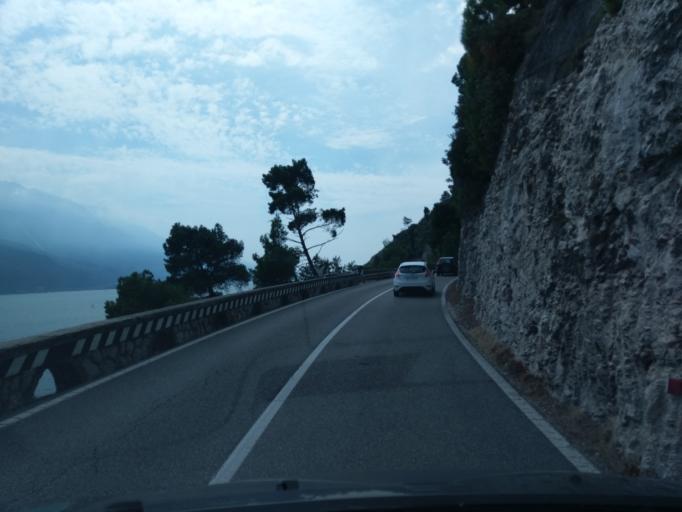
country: IT
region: Lombardy
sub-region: Provincia di Brescia
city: Limone sul Garda
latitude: 45.8323
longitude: 10.8247
